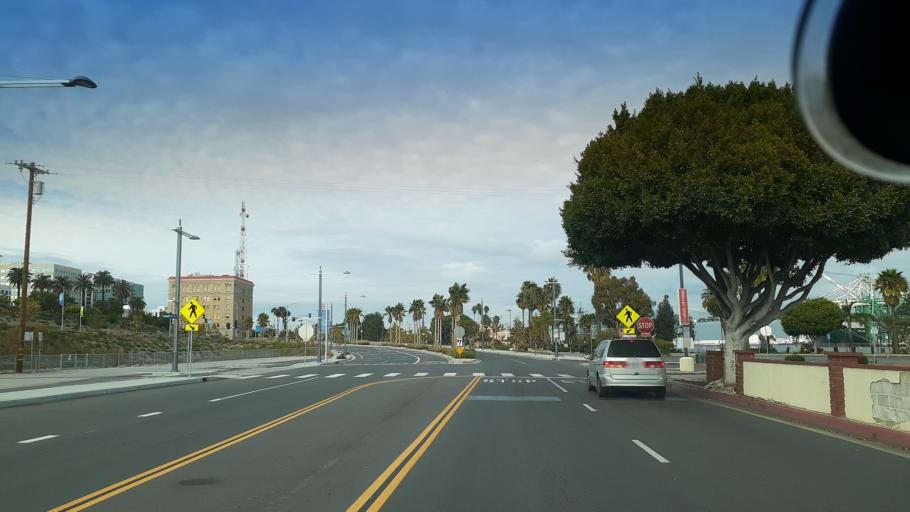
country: US
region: California
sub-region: Los Angeles County
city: San Pedro
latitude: 33.7348
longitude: -118.2790
